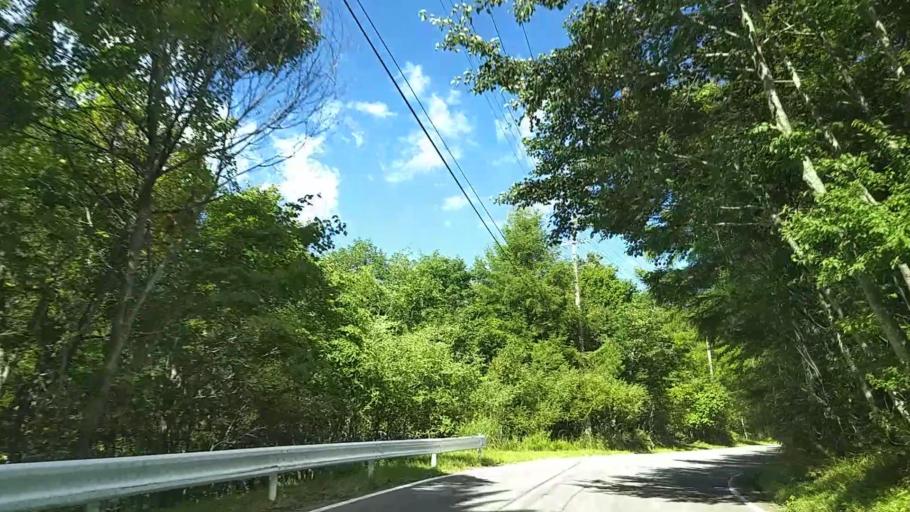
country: JP
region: Nagano
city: Chino
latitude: 36.1197
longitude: 138.2685
